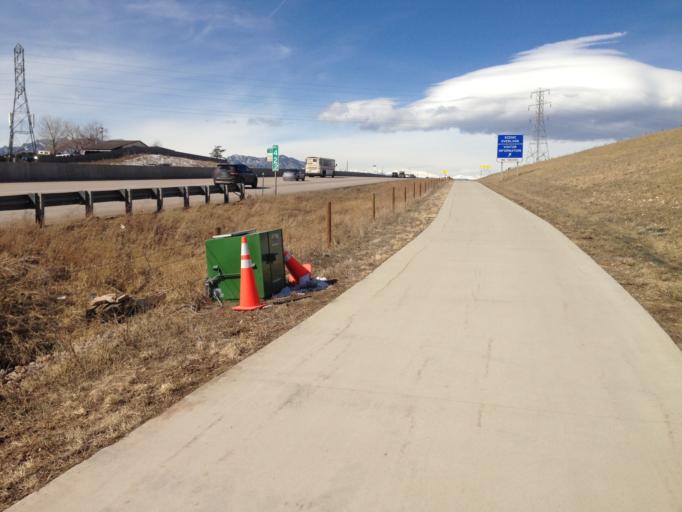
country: US
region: Colorado
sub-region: Boulder County
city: Superior
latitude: 39.9645
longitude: -105.1822
